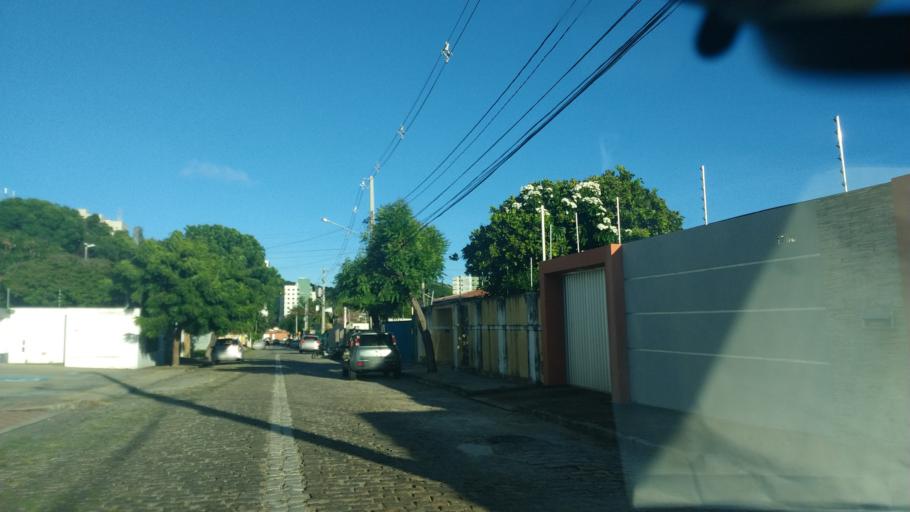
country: BR
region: Rio Grande do Norte
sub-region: Natal
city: Natal
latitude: -5.8127
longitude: -35.2014
